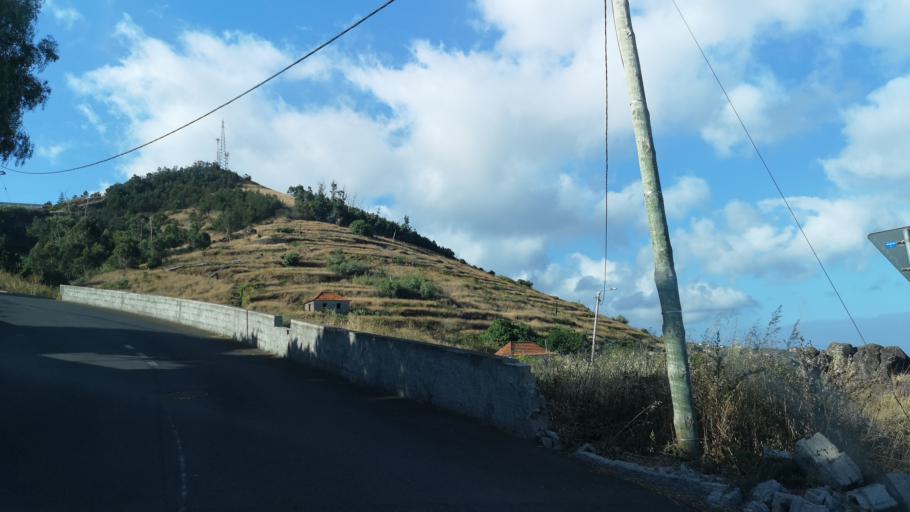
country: PT
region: Madeira
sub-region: Santa Cruz
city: Camacha
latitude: 32.6557
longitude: -16.8342
